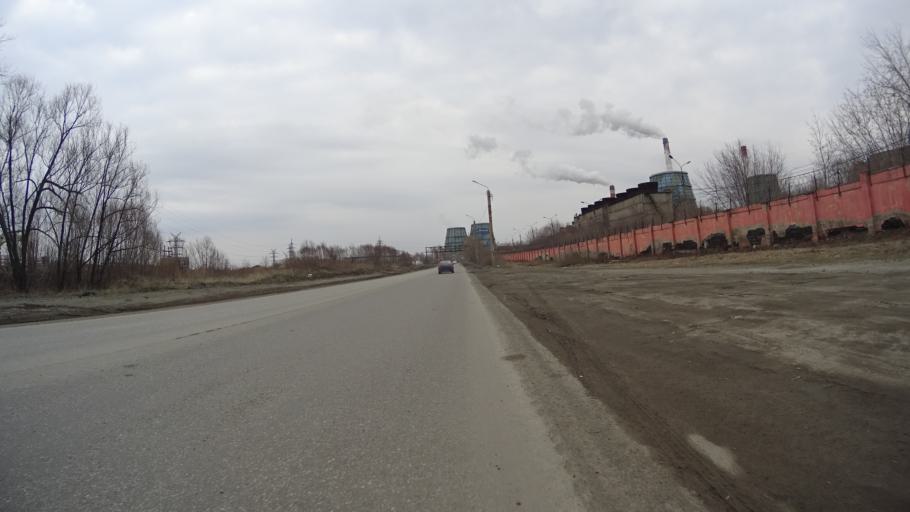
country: RU
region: Chelyabinsk
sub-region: Gorod Chelyabinsk
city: Chelyabinsk
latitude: 55.1574
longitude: 61.4903
